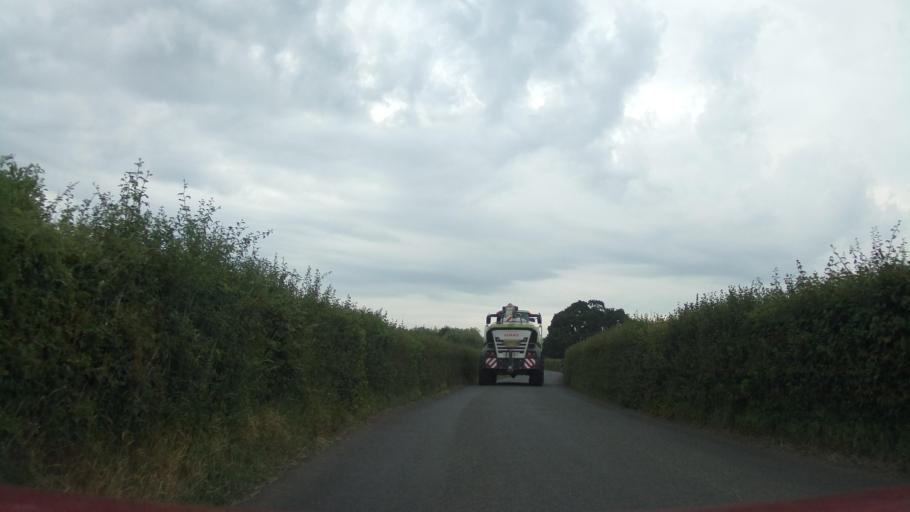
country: GB
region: England
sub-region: Somerset
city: Yeovil
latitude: 50.9131
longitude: -2.5827
